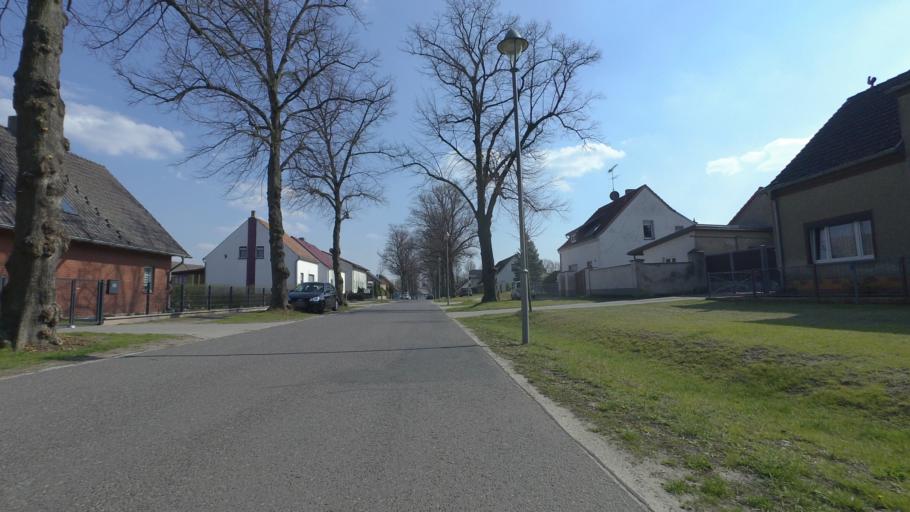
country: DE
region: Brandenburg
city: Teupitz
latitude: 52.1727
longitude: 13.5743
